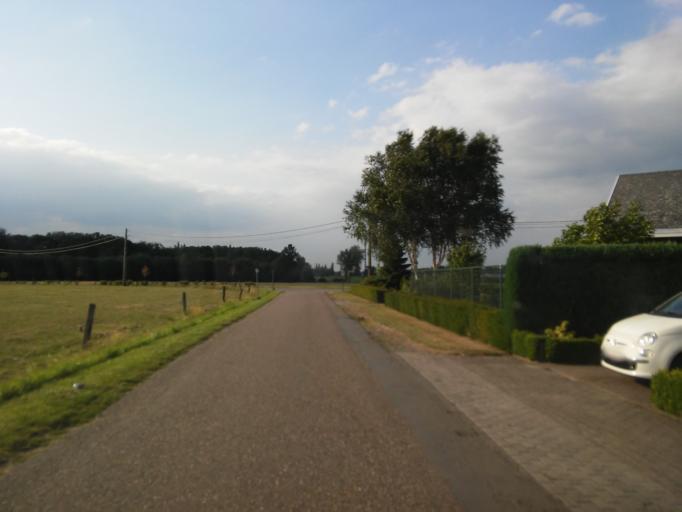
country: BE
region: Flanders
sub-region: Provincie Antwerpen
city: Kontich
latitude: 51.1001
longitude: 4.4617
